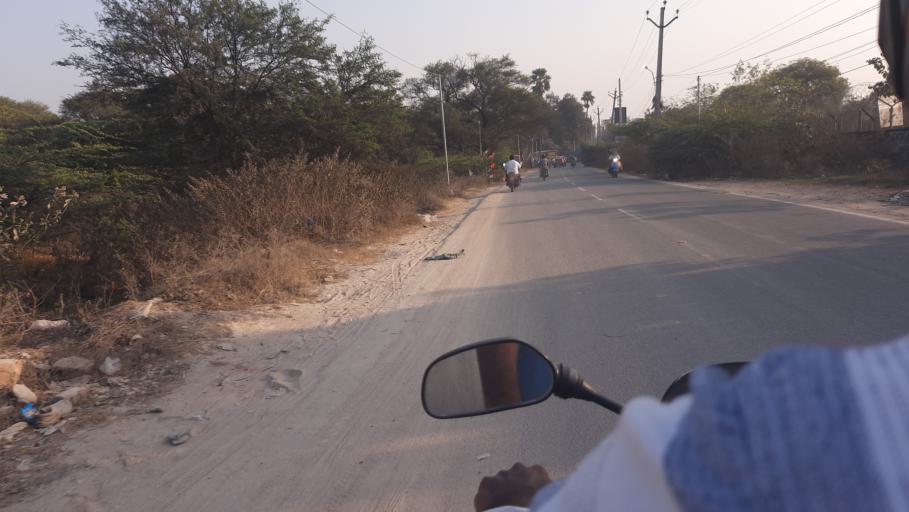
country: IN
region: Telangana
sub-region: Rangareddi
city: Secunderabad
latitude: 17.5128
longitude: 78.5402
